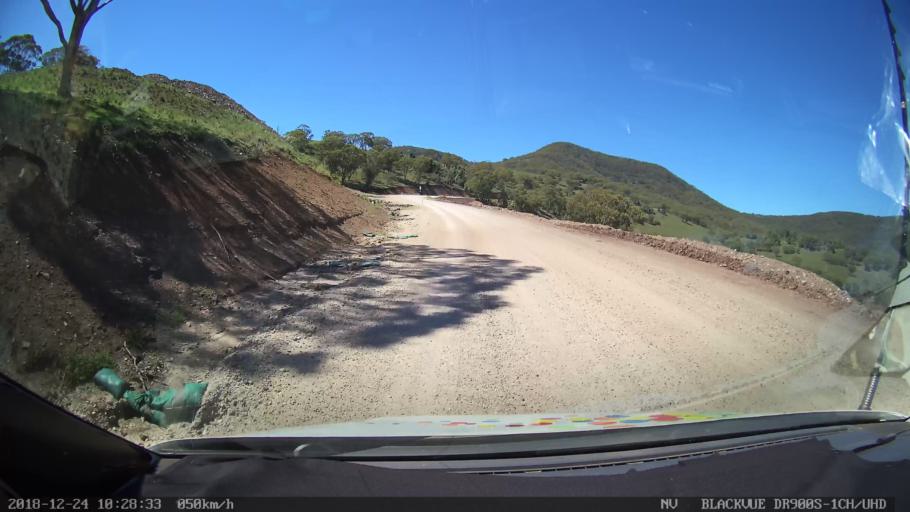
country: AU
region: New South Wales
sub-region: Liverpool Plains
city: Quirindi
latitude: -31.8267
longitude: 150.5313
